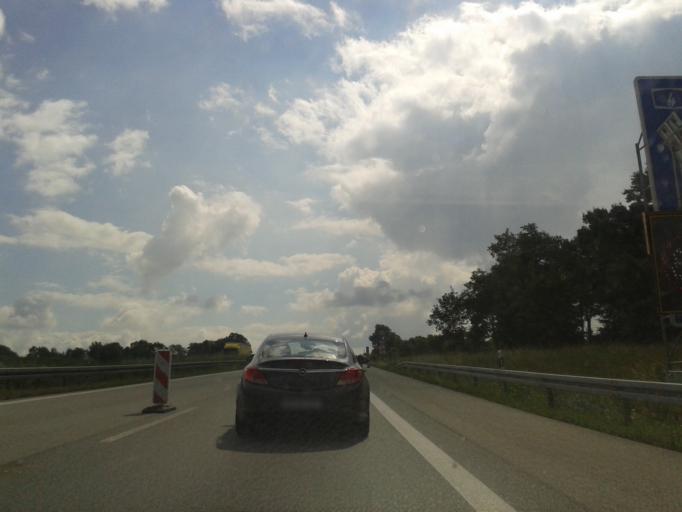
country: DE
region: Saxony
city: Goda
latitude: 51.1957
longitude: 14.3484
